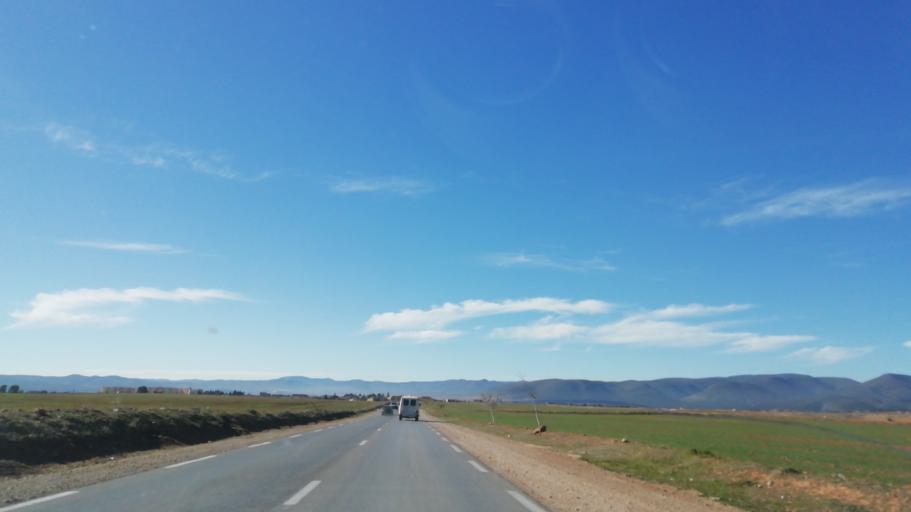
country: DZ
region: Tlemcen
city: Sebdou
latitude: 34.6708
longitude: -1.2767
